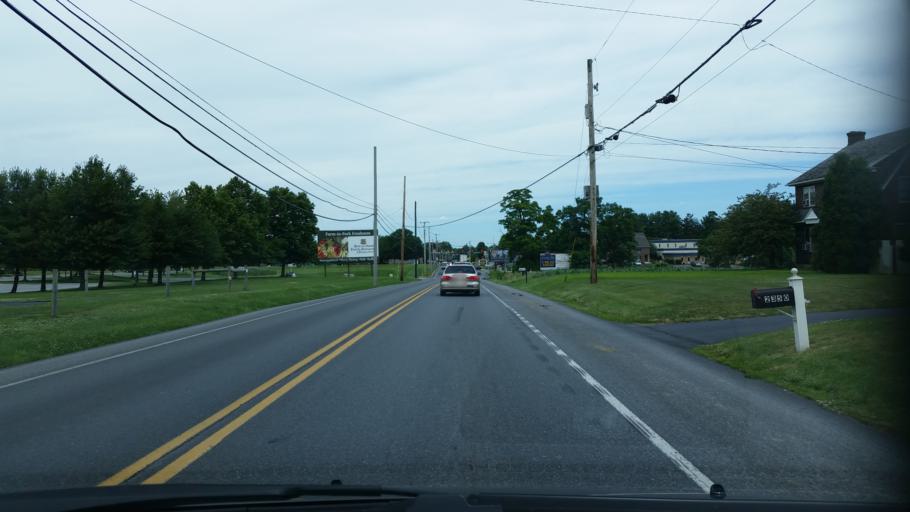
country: US
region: Pennsylvania
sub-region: Lancaster County
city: Lampeter
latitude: 40.0396
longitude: -76.2128
